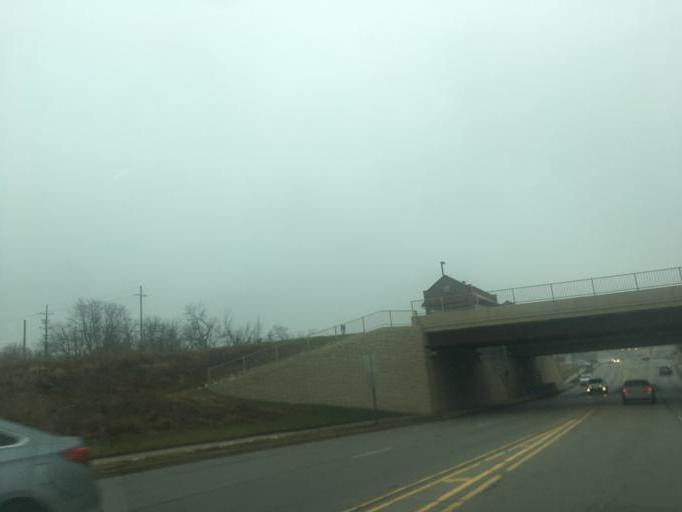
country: US
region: Illinois
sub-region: DuPage County
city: Downers Grove
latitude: 41.7963
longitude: -88.0376
